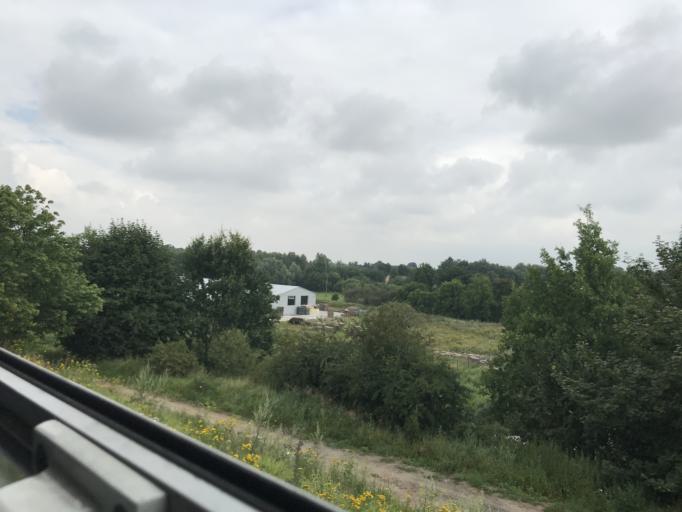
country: PL
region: Pomeranian Voivodeship
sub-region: Powiat malborski
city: Malbork
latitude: 54.0456
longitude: 19.0281
